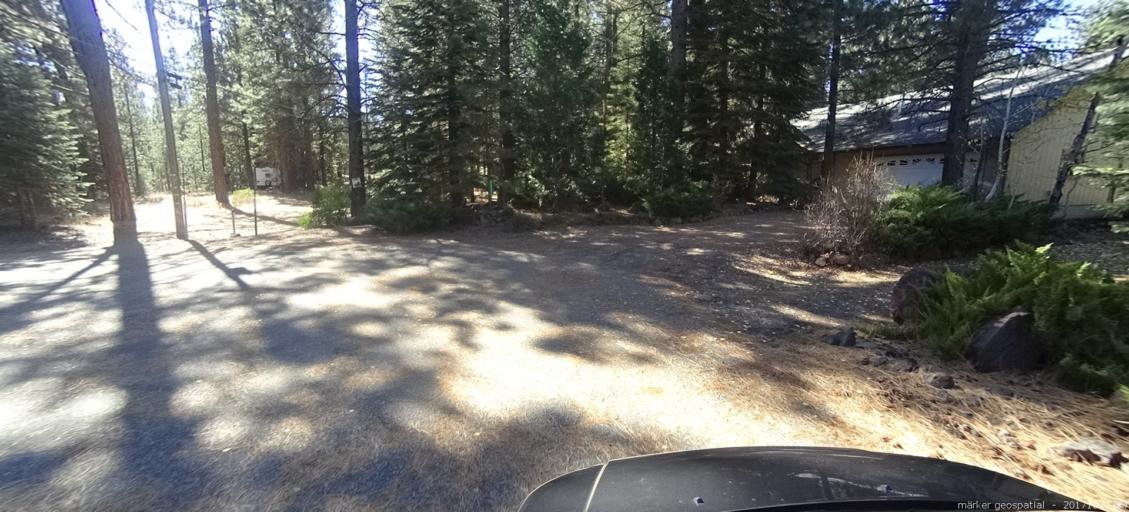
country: US
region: California
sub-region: Shasta County
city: Burney
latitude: 40.6501
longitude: -121.4627
